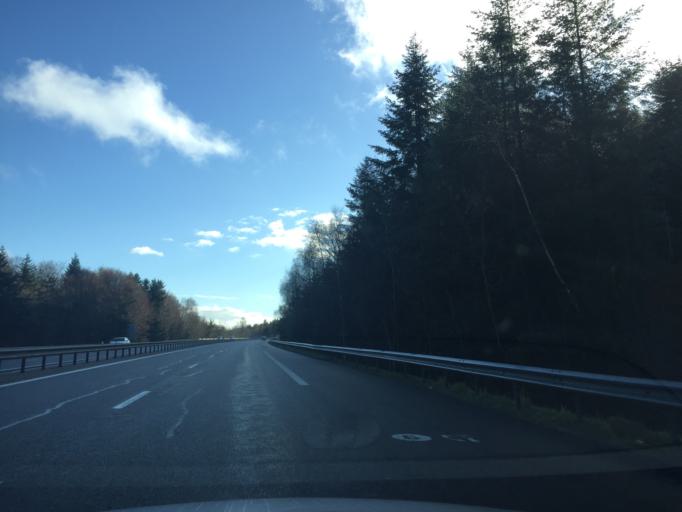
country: FR
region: Auvergne
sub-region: Departement du Puy-de-Dome
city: Chabreloche
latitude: 45.8642
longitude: 3.7185
